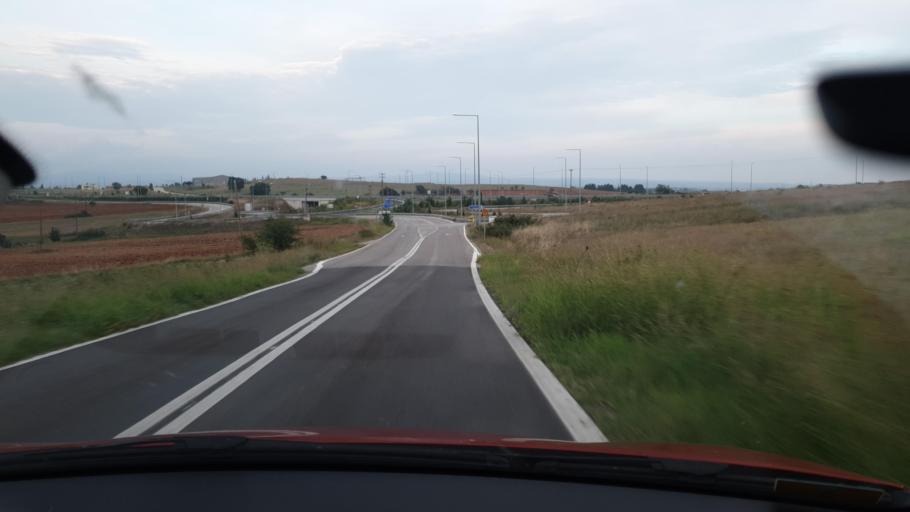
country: GR
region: Central Macedonia
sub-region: Nomos Kilkis
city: Kristoni
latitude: 40.9558
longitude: 22.8443
